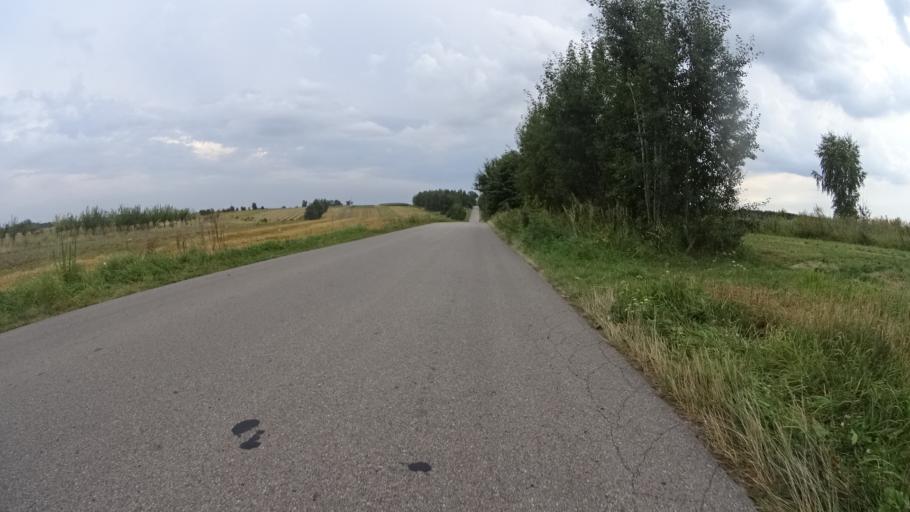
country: PL
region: Masovian Voivodeship
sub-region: Powiat grojecki
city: Goszczyn
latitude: 51.6736
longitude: 20.8580
